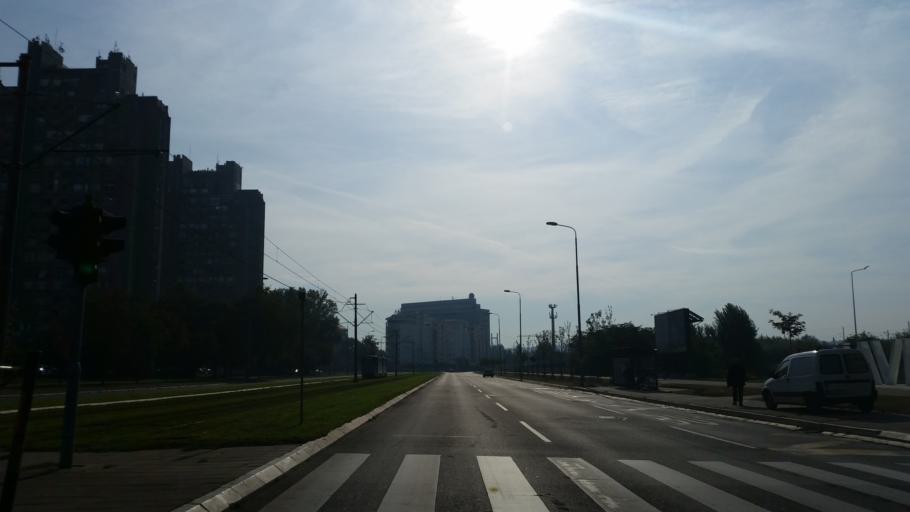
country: RS
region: Central Serbia
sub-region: Belgrade
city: Novi Beograd
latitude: 44.8068
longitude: 20.4225
